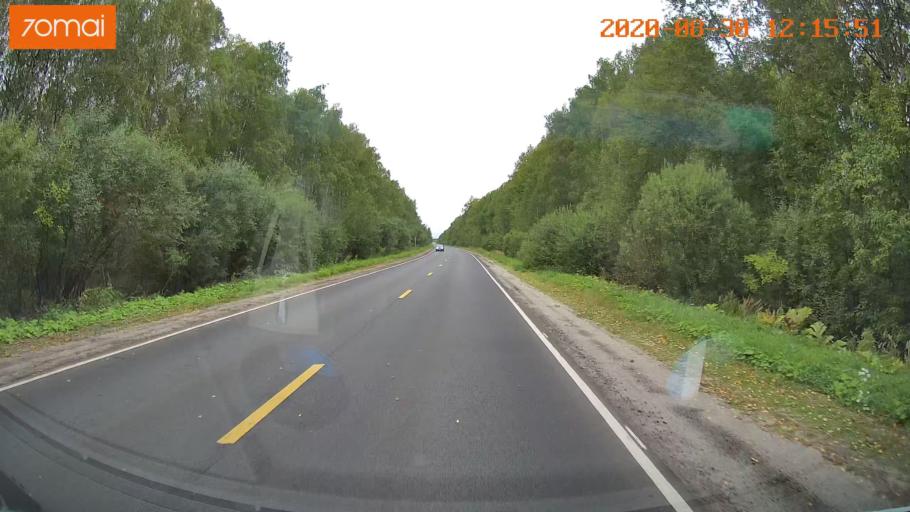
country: RU
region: Ivanovo
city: Yur'yevets
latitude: 57.3187
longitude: 43.0193
